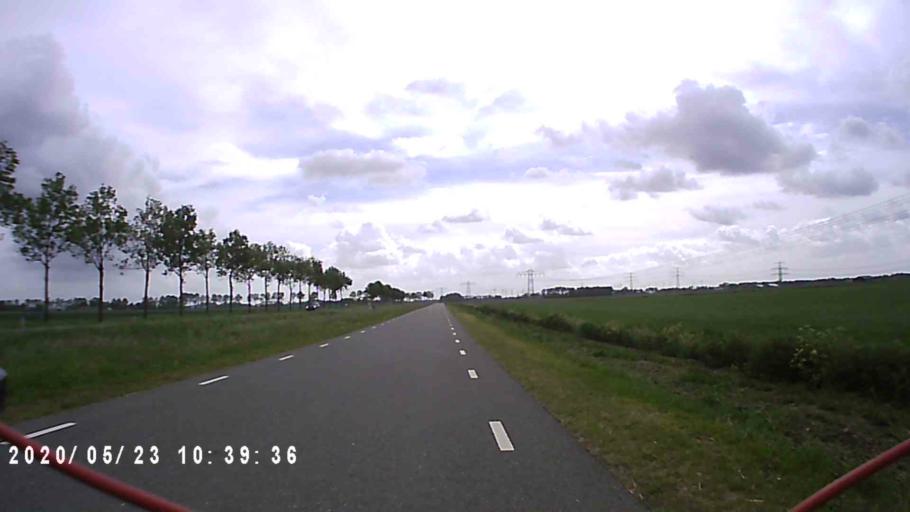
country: NL
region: Groningen
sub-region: Gemeente Appingedam
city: Appingedam
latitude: 53.3029
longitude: 6.8861
